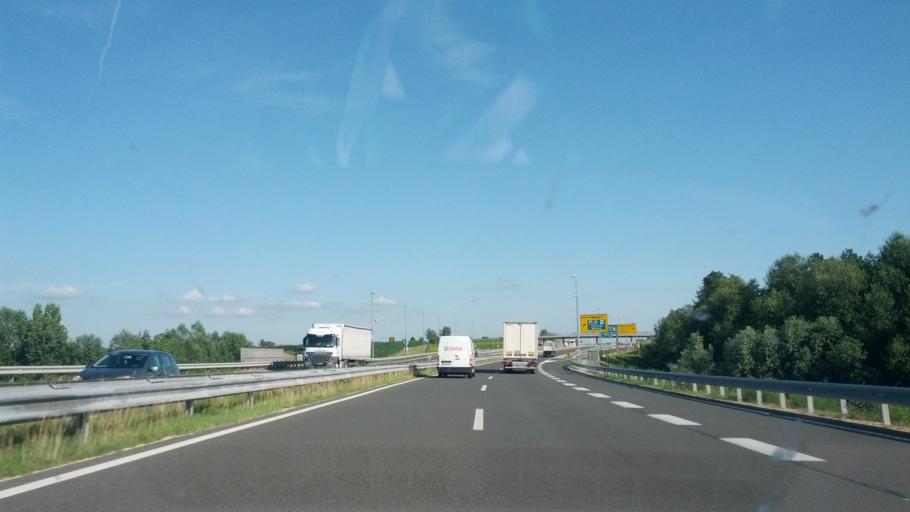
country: HR
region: Zagrebacka
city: Bregana
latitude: 45.8607
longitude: 15.6814
